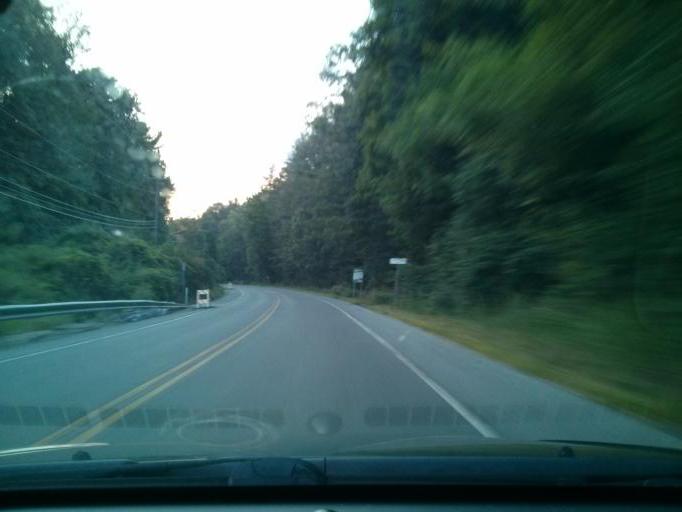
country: US
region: Pennsylvania
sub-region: Centre County
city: State College
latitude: 40.8248
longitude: -77.8693
